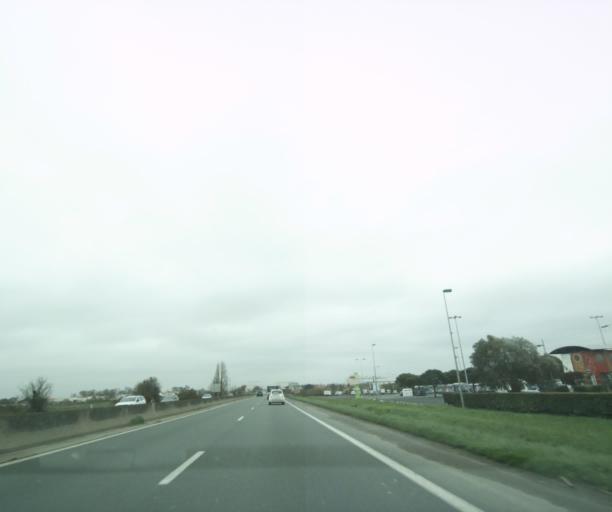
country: FR
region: Poitou-Charentes
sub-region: Departement de la Charente-Maritime
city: Lagord
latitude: 46.1754
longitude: -1.1705
